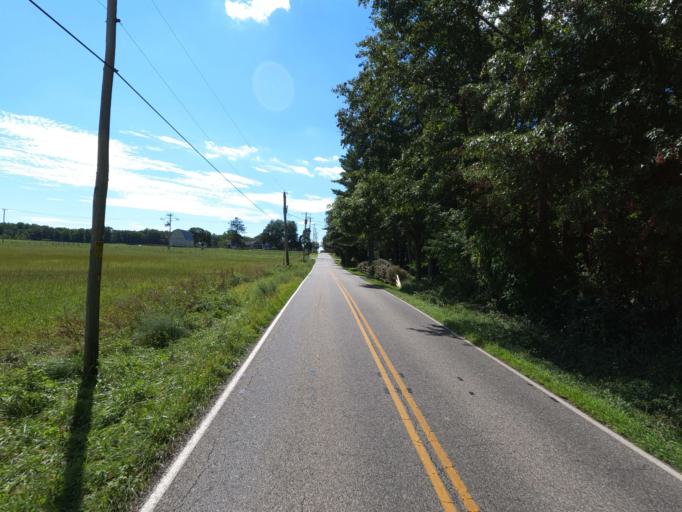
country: US
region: Delaware
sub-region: New Castle County
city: Glasgow
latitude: 39.5891
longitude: -75.7891
